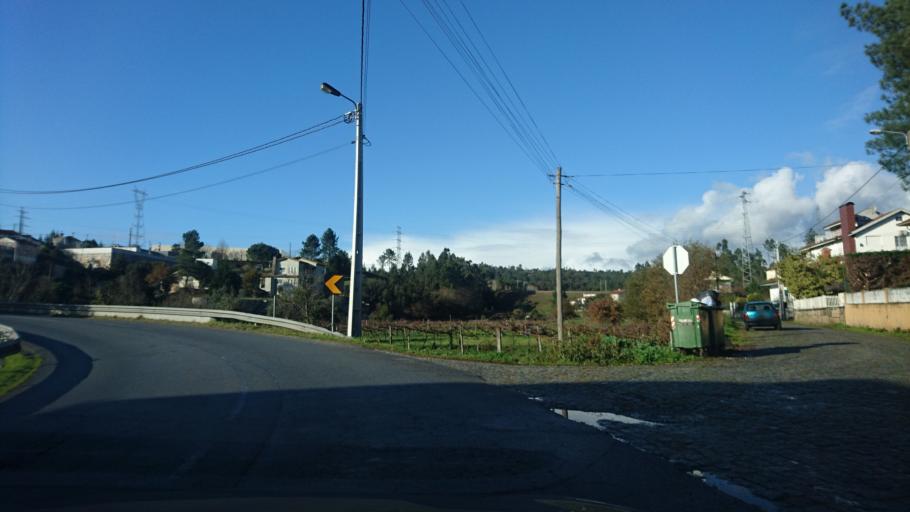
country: PT
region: Porto
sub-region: Paredes
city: Recarei
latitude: 41.1581
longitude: -8.4205
